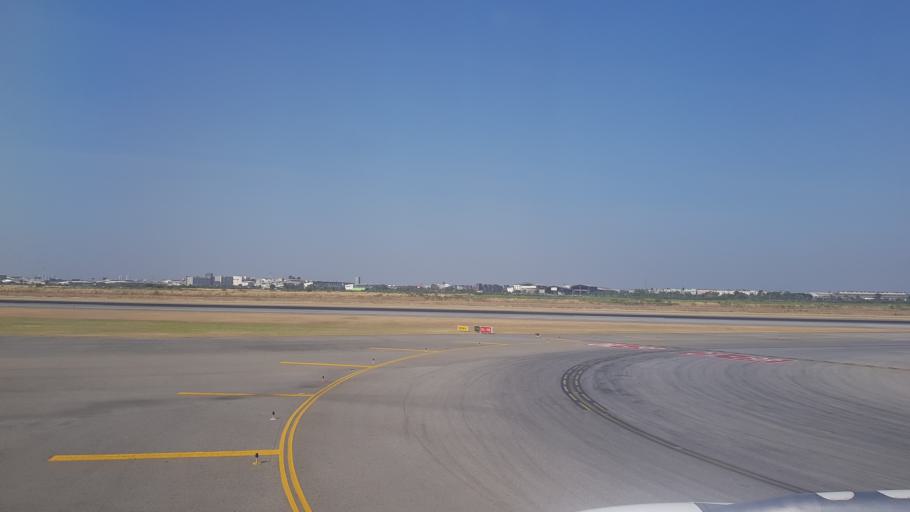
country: TH
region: Bangkok
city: Lat Krabang
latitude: 13.6786
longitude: 100.7385
